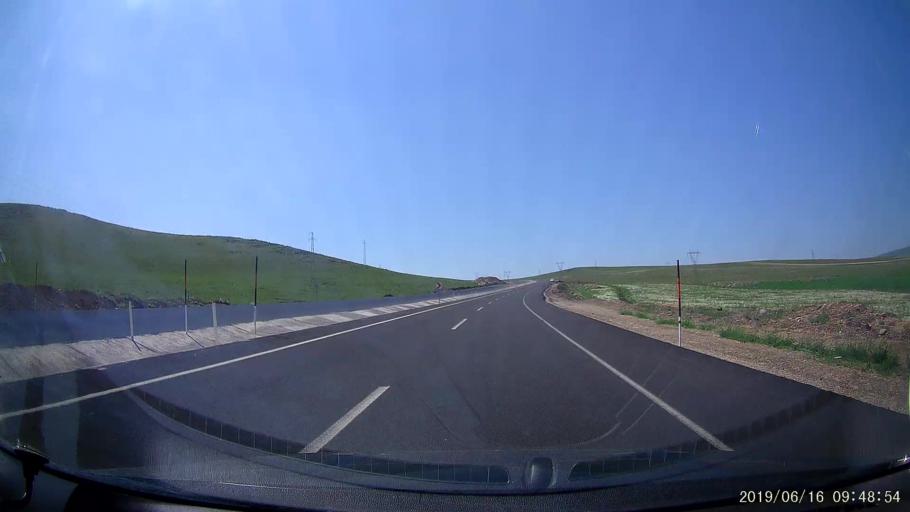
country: TR
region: Kars
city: Digor
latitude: 40.4281
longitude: 43.3560
